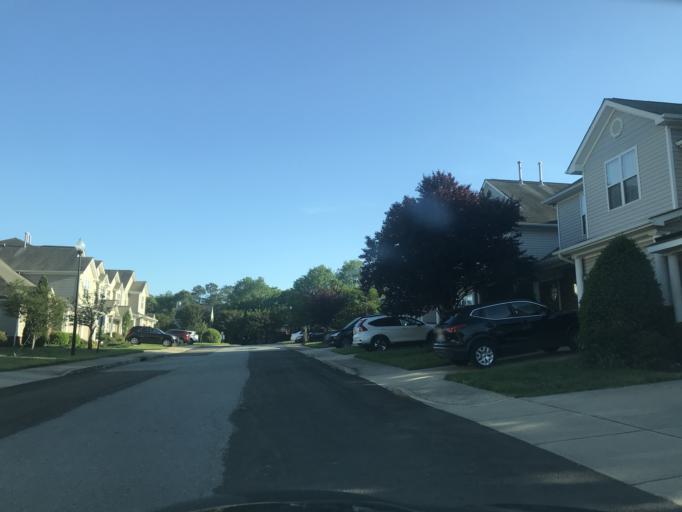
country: US
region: North Carolina
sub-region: Wake County
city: Raleigh
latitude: 35.8209
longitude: -78.5673
